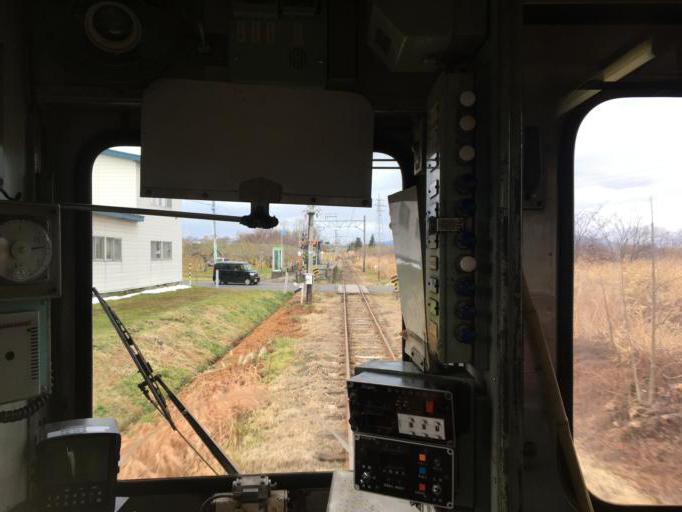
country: JP
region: Aomori
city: Hirosaki
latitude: 40.5604
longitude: 140.4980
